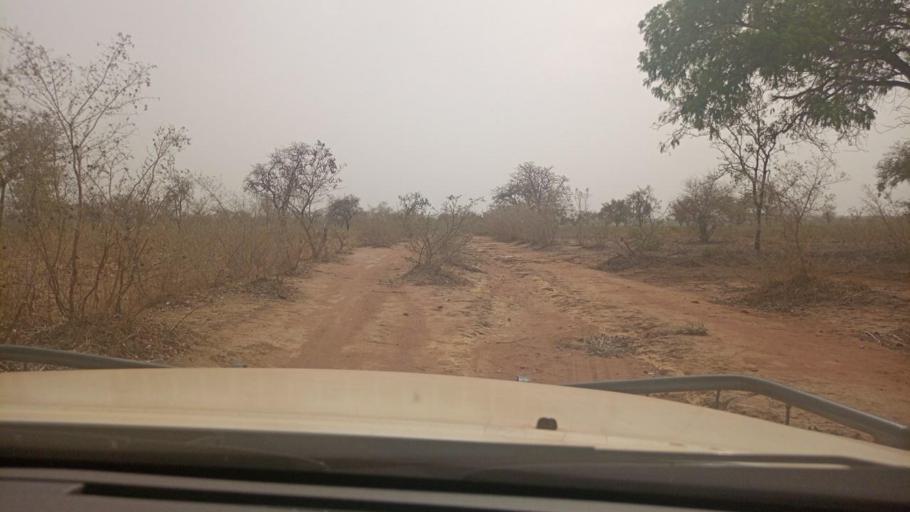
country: BF
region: Boucle du Mouhoun
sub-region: Province des Banwa
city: Salanso
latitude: 12.1648
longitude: -4.2371
